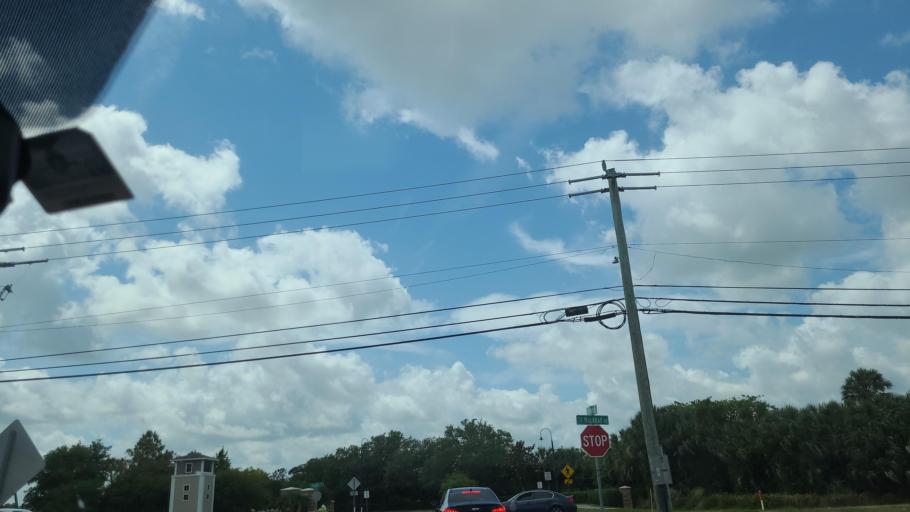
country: US
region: Florida
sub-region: Brevard County
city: June Park
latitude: 27.9994
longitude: -80.6805
